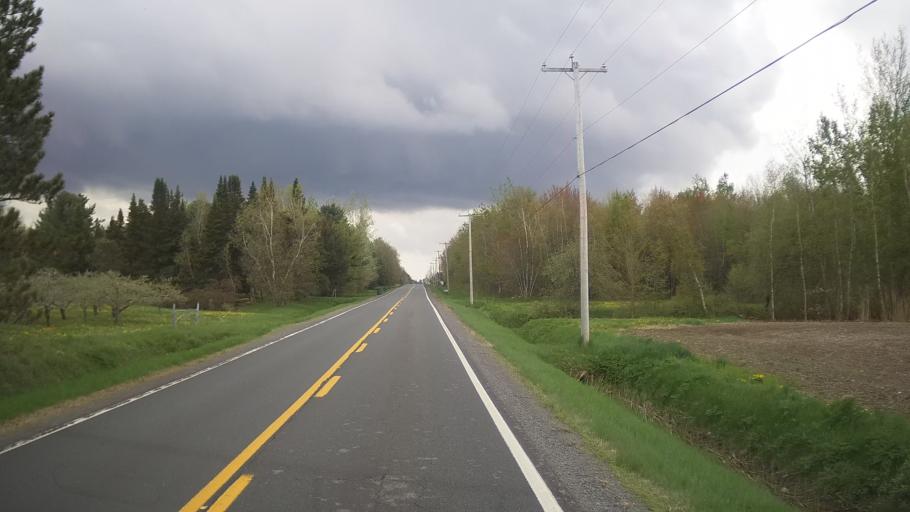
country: CA
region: Quebec
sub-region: Monteregie
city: Marieville
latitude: 45.3234
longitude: -73.1085
